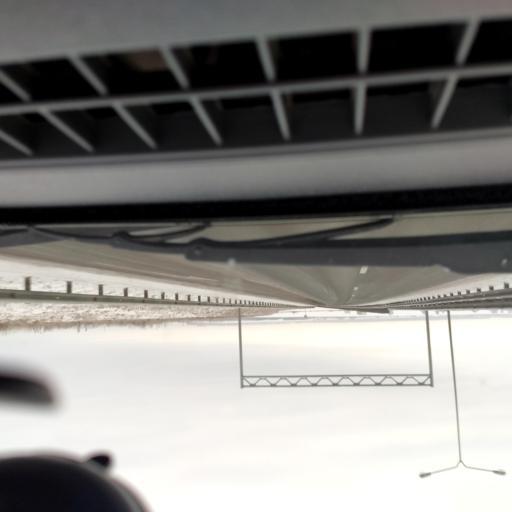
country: RU
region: Bashkortostan
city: Kushnarenkovo
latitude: 55.0649
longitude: 55.3119
